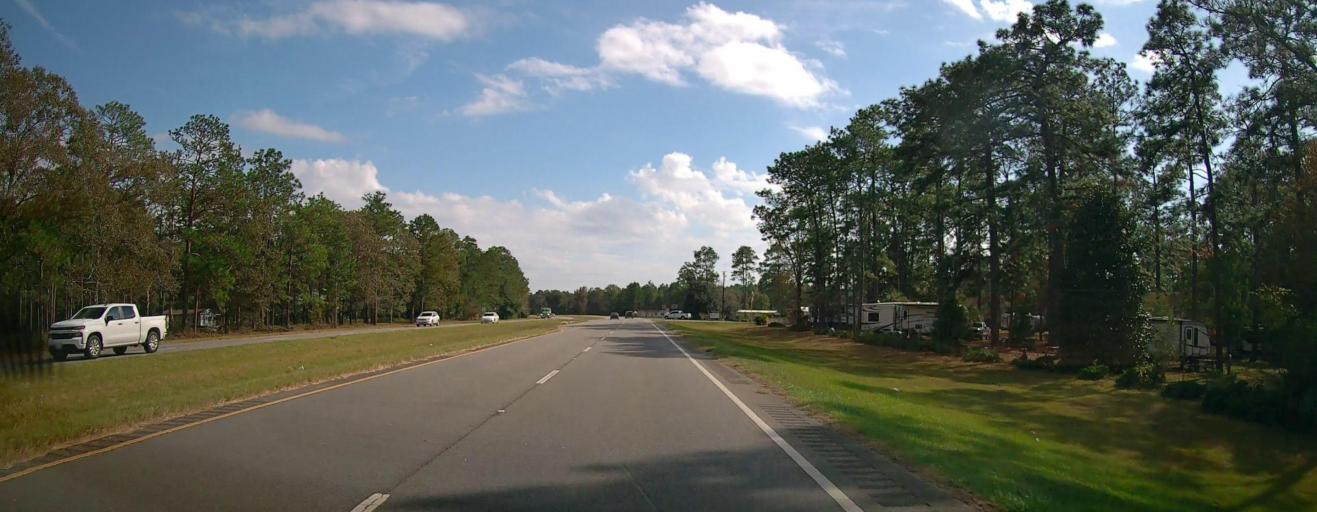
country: US
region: Georgia
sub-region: Thomas County
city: Thomasville
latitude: 30.9512
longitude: -84.0249
